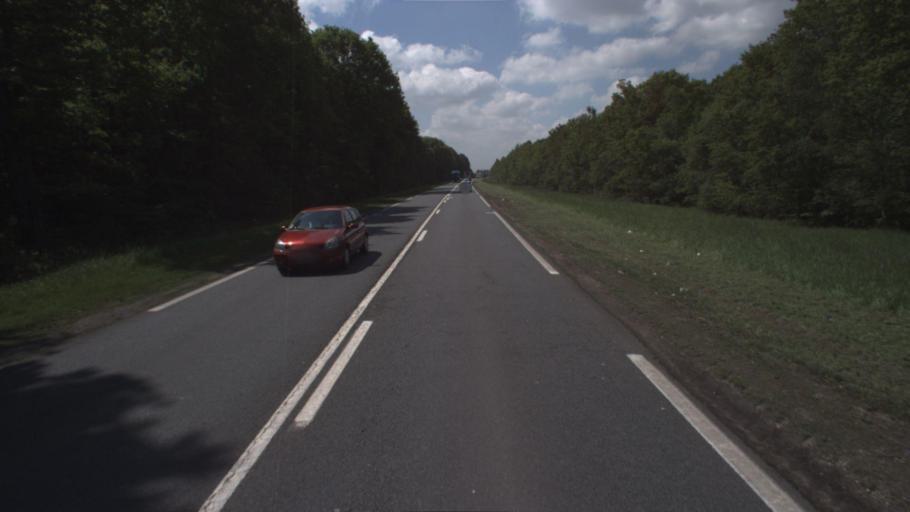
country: FR
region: Ile-de-France
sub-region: Departement de Seine-et-Marne
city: Guignes
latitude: 48.6495
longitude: 2.8023
